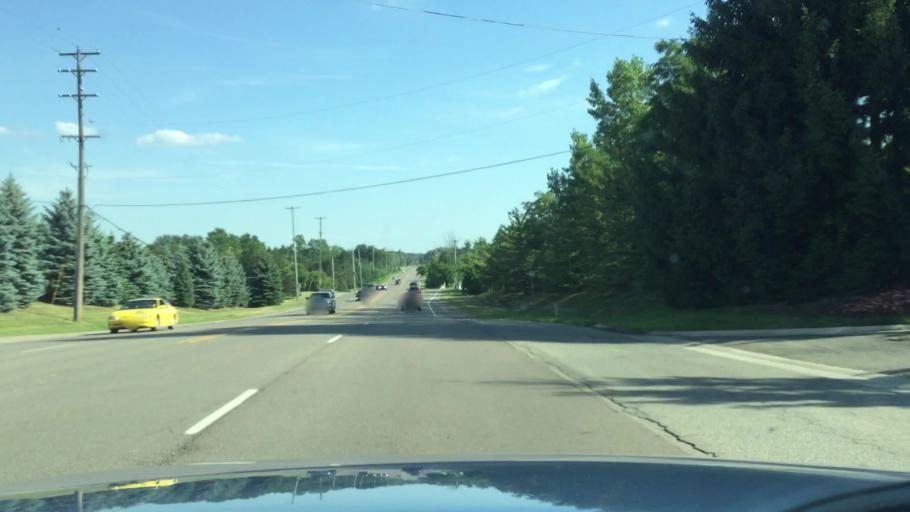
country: US
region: Michigan
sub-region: Genesee County
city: Grand Blanc
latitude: 42.8958
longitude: -83.6012
